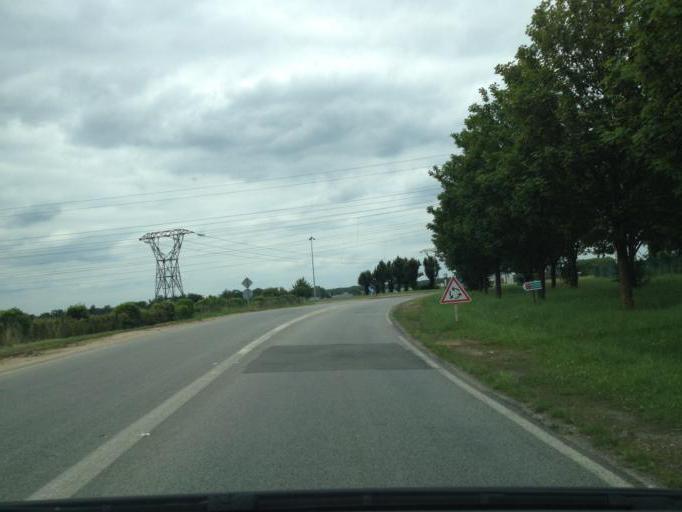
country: FR
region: Ile-de-France
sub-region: Departement des Yvelines
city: Jouy-en-Josas
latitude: 48.7490
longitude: 2.1656
